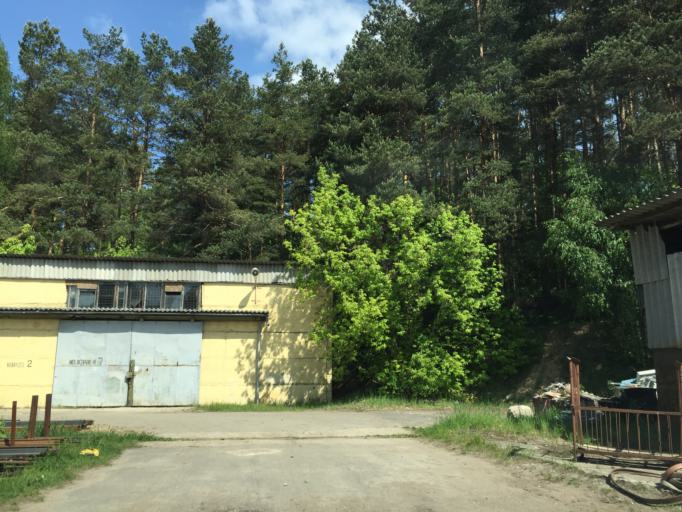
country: LV
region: Riga
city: Bergi
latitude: 56.9998
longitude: 24.2702
